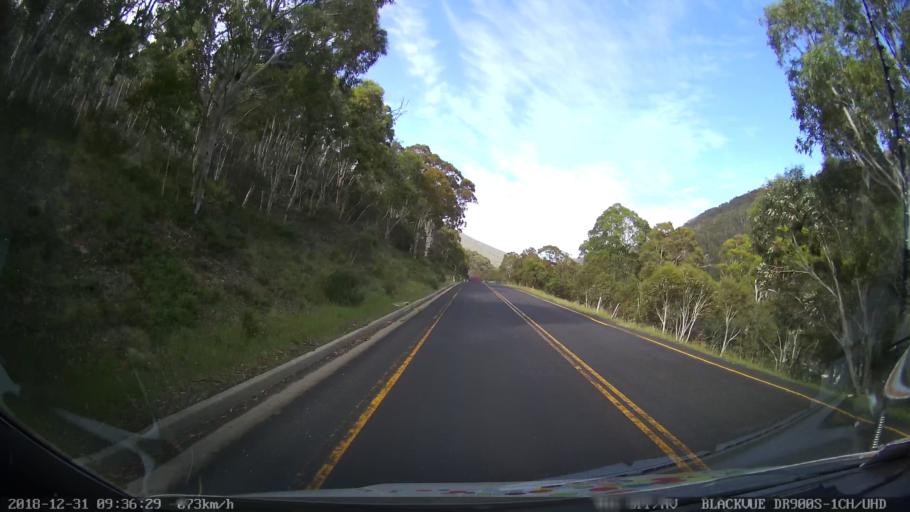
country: AU
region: New South Wales
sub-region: Snowy River
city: Jindabyne
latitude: -36.4589
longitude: 148.3861
